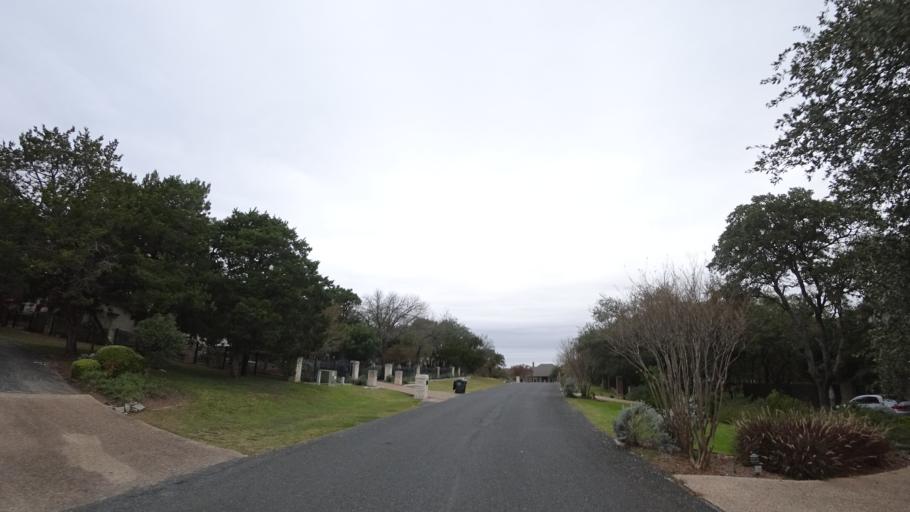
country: US
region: Texas
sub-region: Williamson County
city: Jollyville
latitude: 30.3768
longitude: -97.8161
